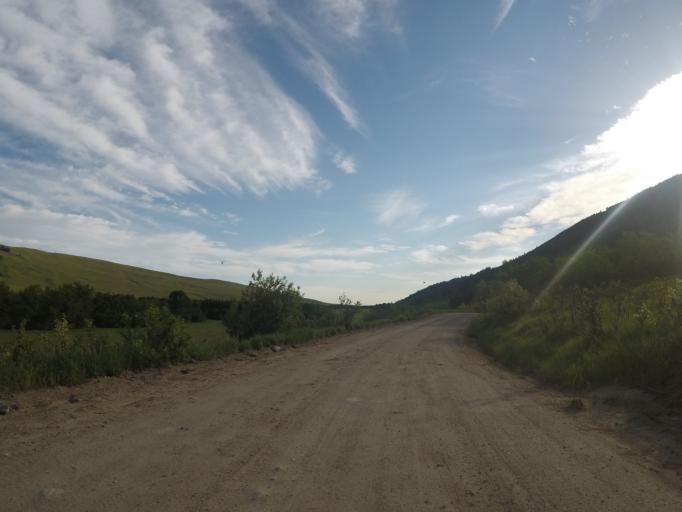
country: US
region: Montana
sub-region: Stillwater County
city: Absarokee
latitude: 45.2797
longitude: -109.5485
